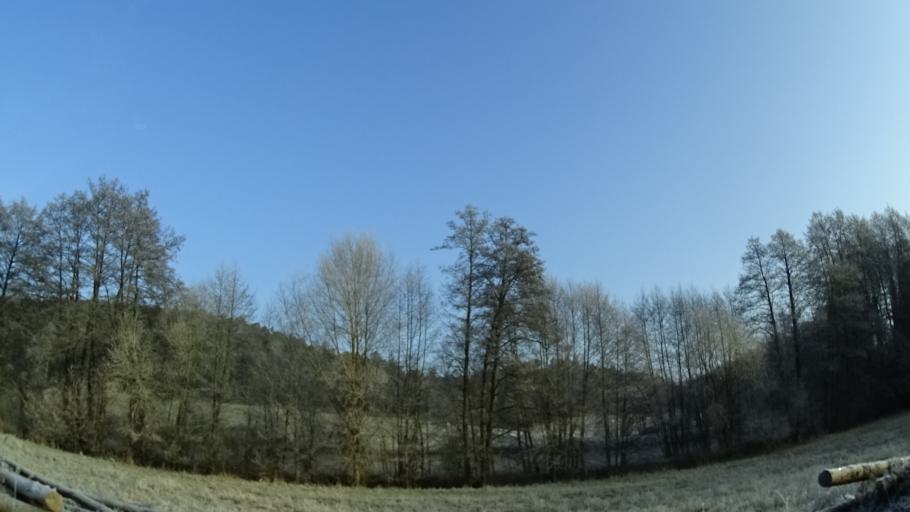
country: DE
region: Bavaria
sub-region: Upper Franconia
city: Weitramsdorf
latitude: 50.2433
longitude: 10.8938
